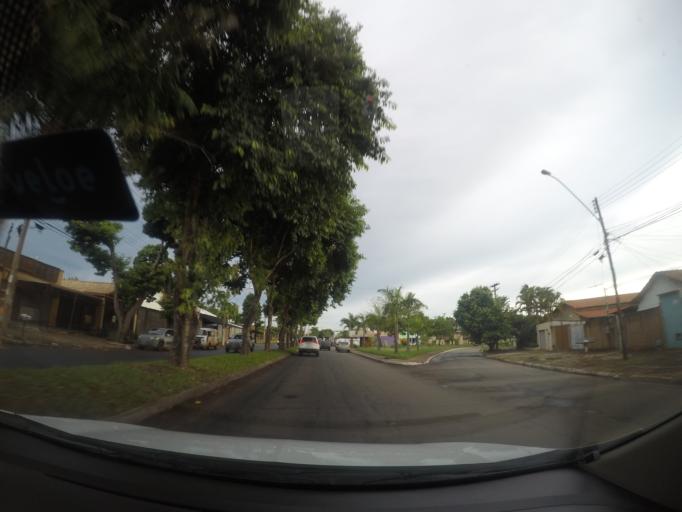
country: BR
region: Goias
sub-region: Goiania
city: Goiania
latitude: -16.7162
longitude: -49.3105
